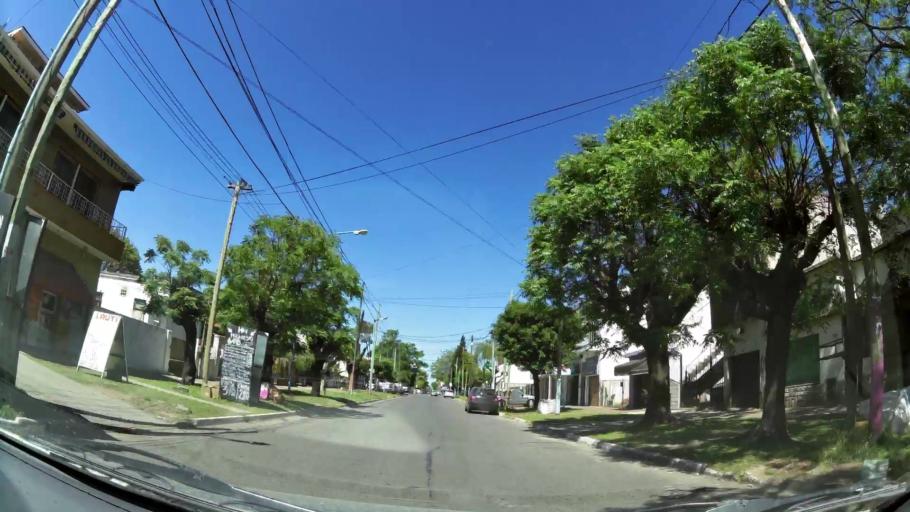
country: AR
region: Buenos Aires
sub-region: Partido de Quilmes
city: Quilmes
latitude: -34.7154
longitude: -58.3037
